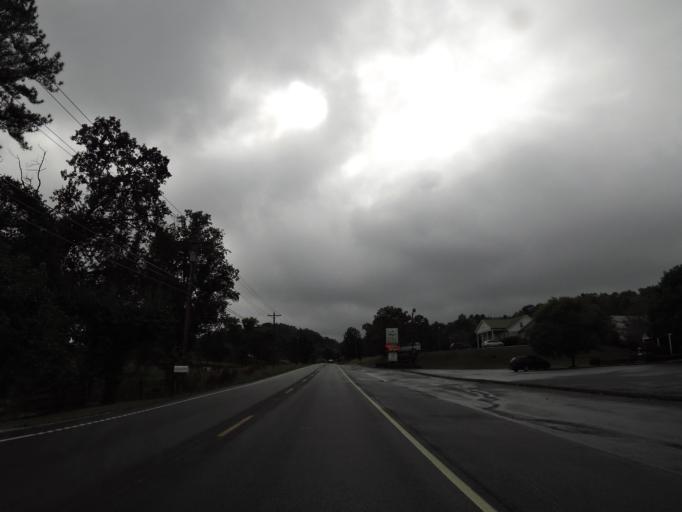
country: US
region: Tennessee
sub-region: Bradley County
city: Cleveland
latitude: 35.1862
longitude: -84.9447
